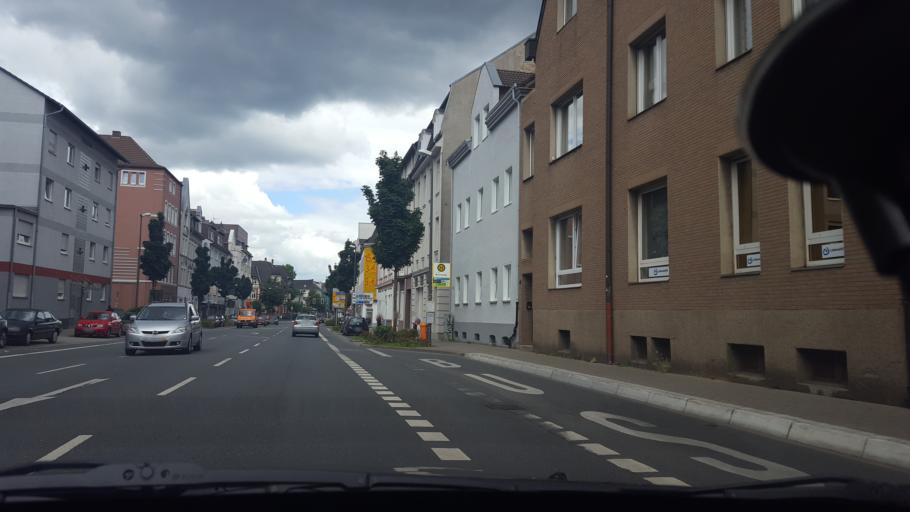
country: DE
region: North Rhine-Westphalia
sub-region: Regierungsbezirk Munster
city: Recklinghausen
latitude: 51.6073
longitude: 7.1990
